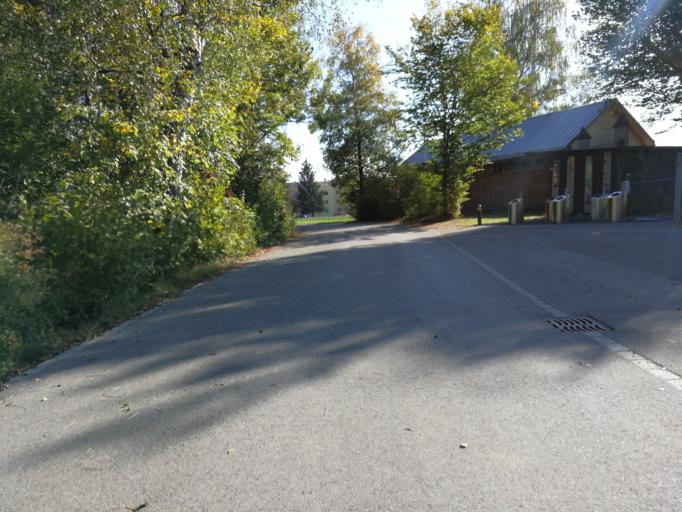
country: CH
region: Zurich
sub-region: Bezirk Uster
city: Monchaltorf
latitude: 47.3141
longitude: 8.7162
